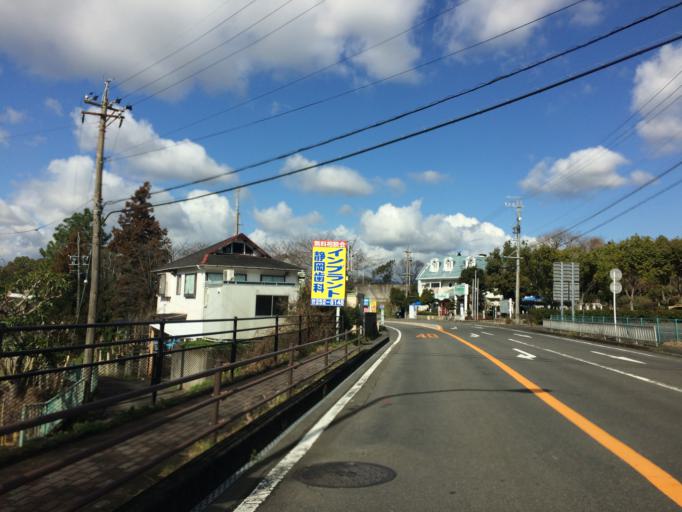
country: JP
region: Shizuoka
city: Shizuoka-shi
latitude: 34.9816
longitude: 138.4351
